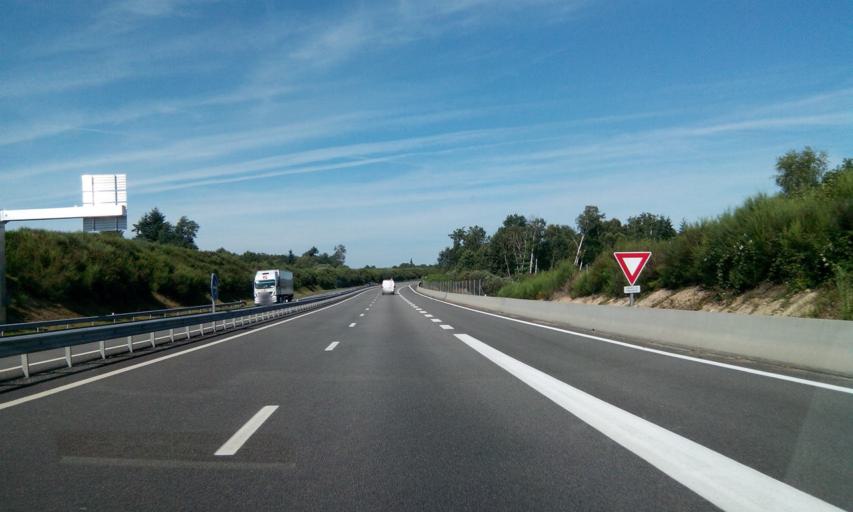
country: FR
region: Limousin
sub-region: Departement de la Haute-Vienne
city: Veyrac
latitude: 45.8833
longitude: 1.0924
